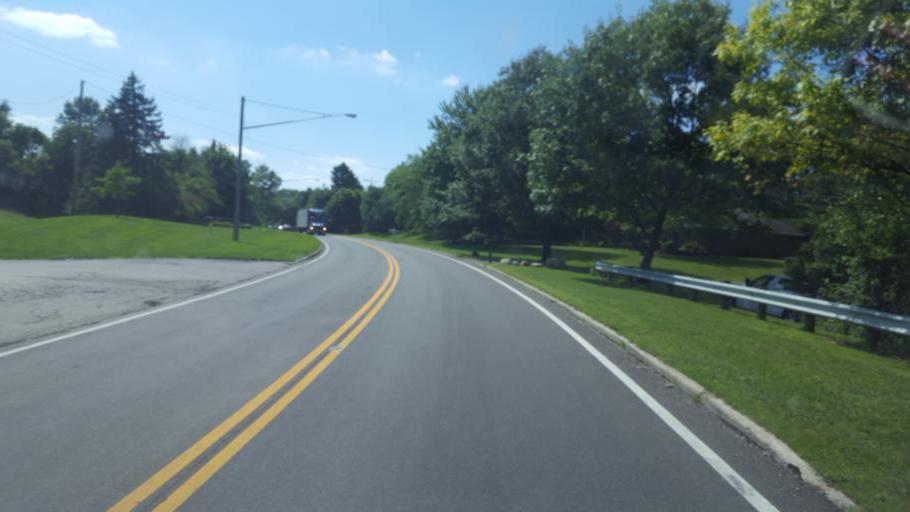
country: US
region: Ohio
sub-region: Franklin County
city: Minerva Park
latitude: 40.0365
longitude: -82.9367
